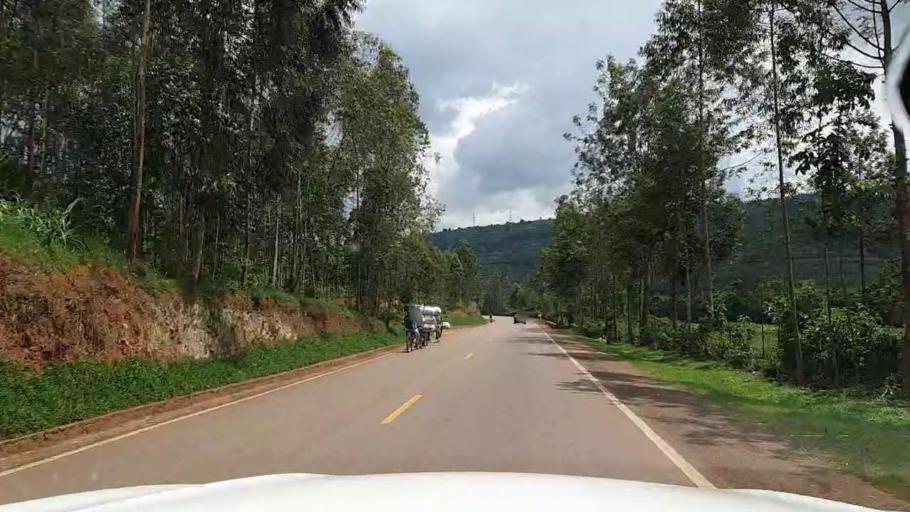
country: RW
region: Kigali
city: Kigali
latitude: -1.8038
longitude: 30.1267
